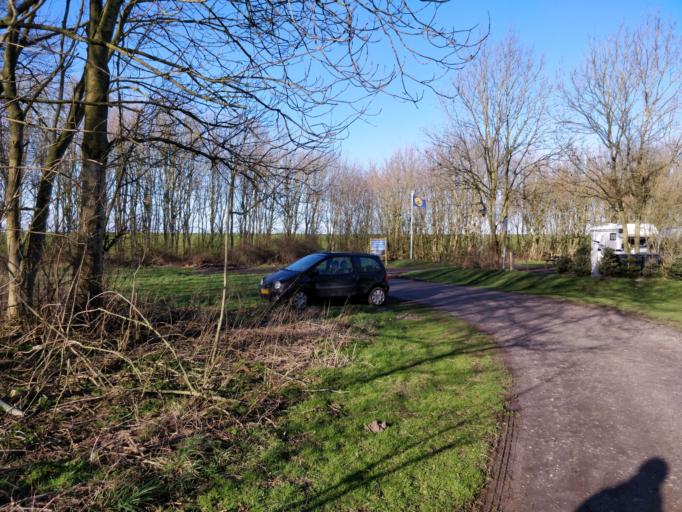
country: NL
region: Friesland
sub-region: Gemeente Het Bildt
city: Sint Annaparochie
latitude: 53.3088
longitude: 5.6296
